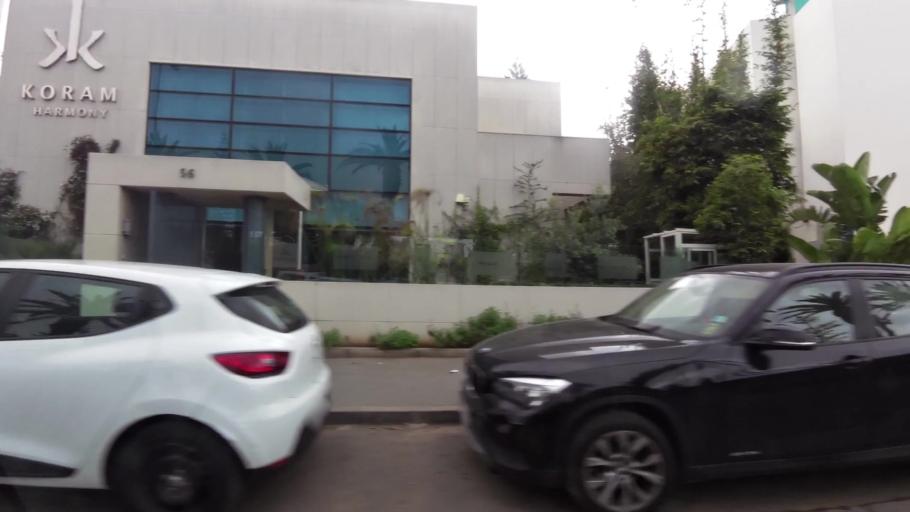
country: MA
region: Grand Casablanca
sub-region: Casablanca
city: Casablanca
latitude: 33.5798
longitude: -7.6566
